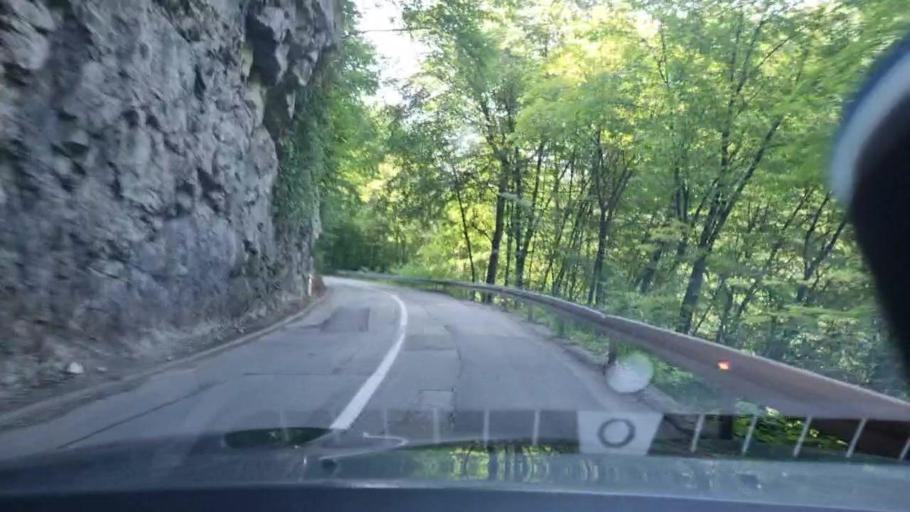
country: BA
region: Federation of Bosnia and Herzegovina
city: Stijena
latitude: 44.8899
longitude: 16.0530
